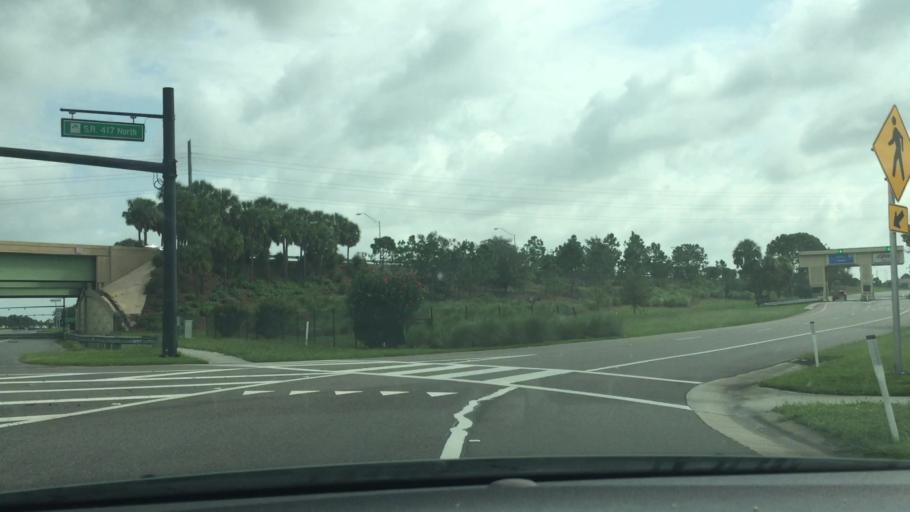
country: US
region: Florida
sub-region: Orange County
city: Hunters Creek
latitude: 28.3667
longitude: -81.4240
